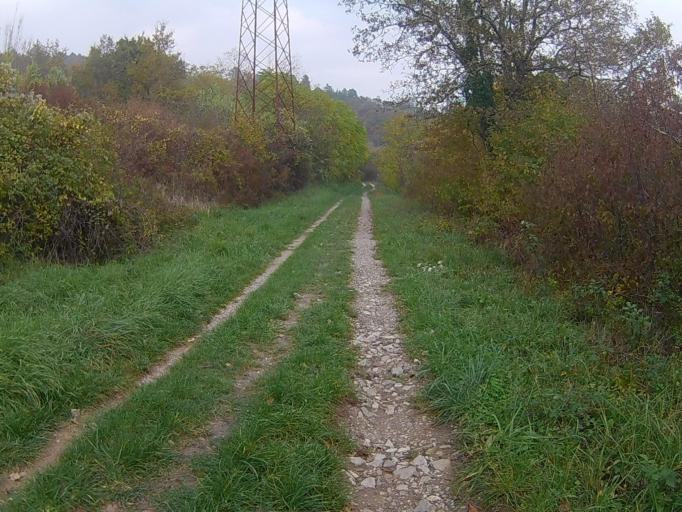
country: HR
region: Istarska
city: Karojba
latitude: 45.3577
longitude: 13.7893
